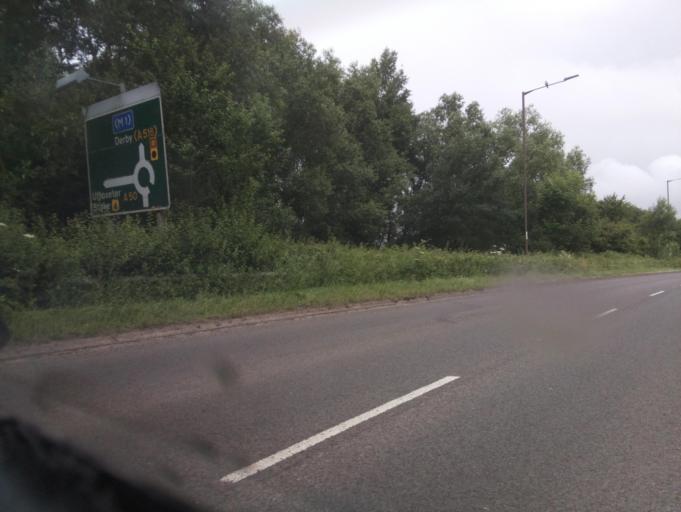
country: GB
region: England
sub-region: Derbyshire
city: Rodsley
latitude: 52.8787
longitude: -1.6997
